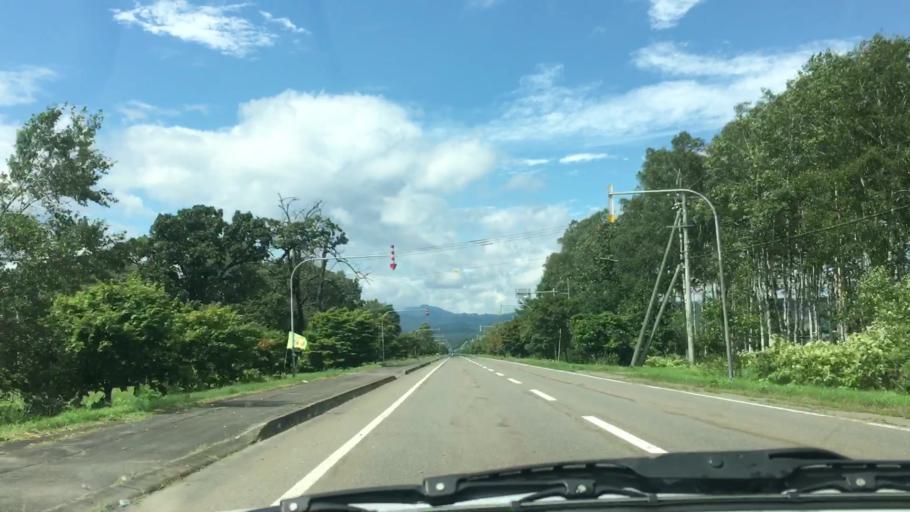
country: JP
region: Hokkaido
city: Otofuke
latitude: 43.3064
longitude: 143.3109
